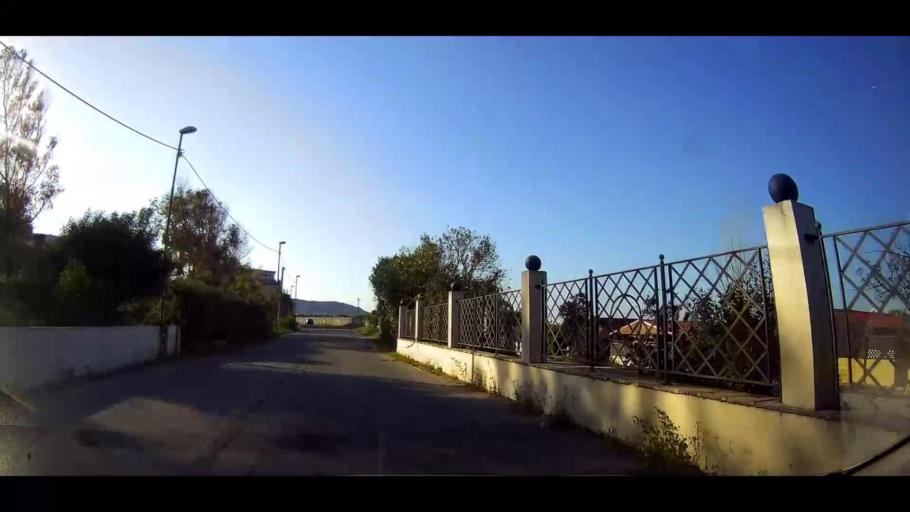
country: IT
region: Calabria
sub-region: Provincia di Crotone
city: Crotone
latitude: 39.0488
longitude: 17.1442
